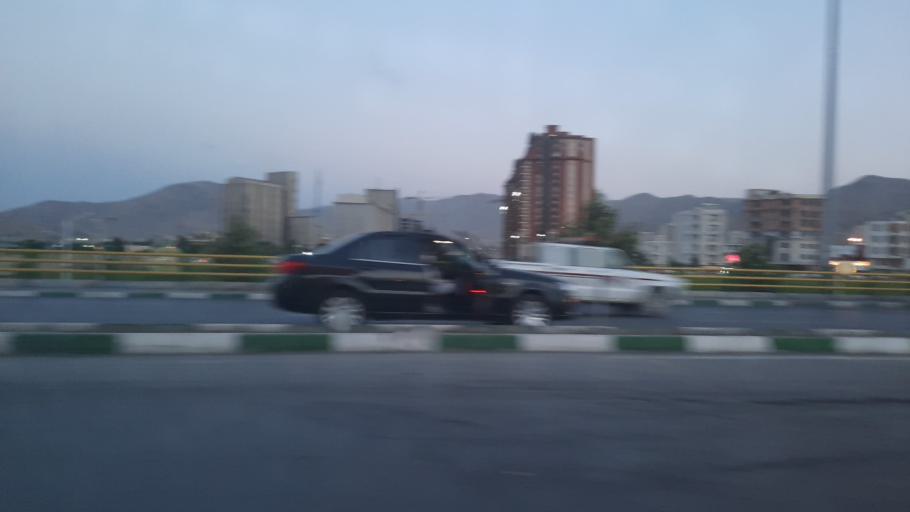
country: IR
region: Markazi
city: Arak
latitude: 34.0854
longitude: 49.7055
